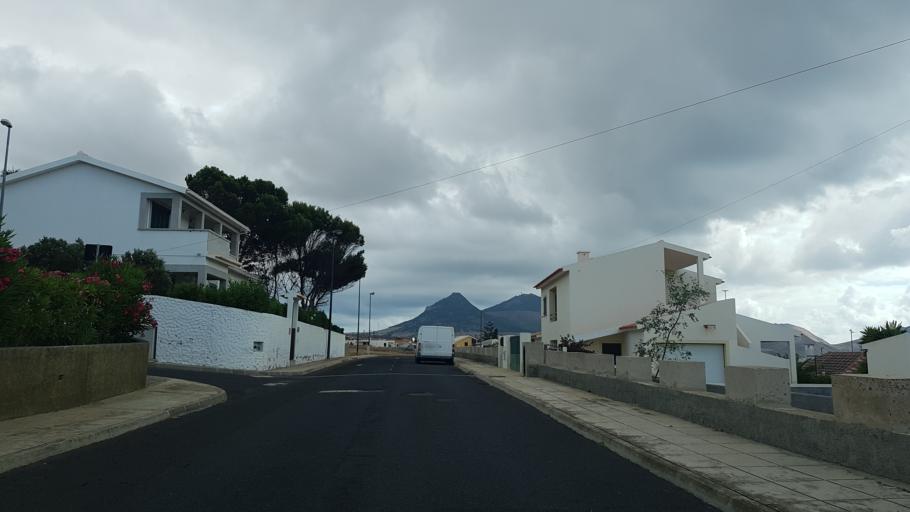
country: PT
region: Madeira
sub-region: Porto Santo
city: Vila de Porto Santo
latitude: 33.0407
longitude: -16.3612
